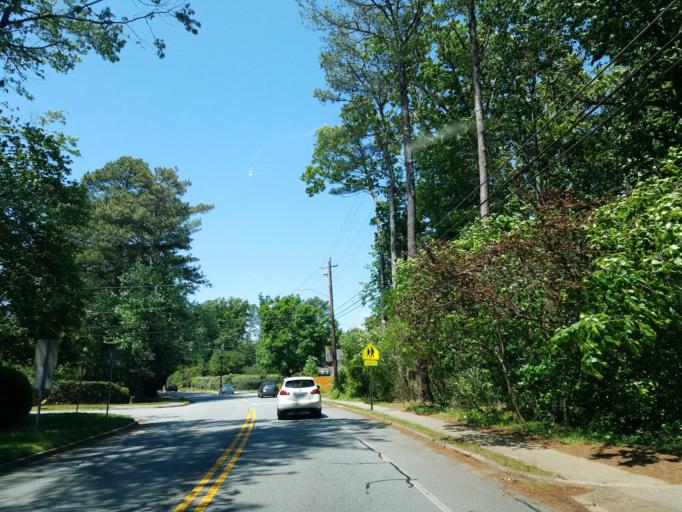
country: US
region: Georgia
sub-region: DeKalb County
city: Dunwoody
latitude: 33.9570
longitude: -84.3359
